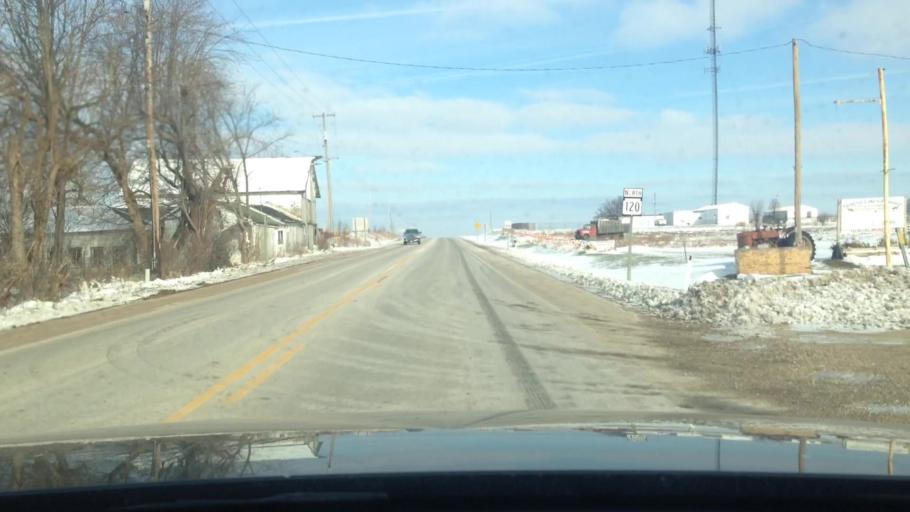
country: US
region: Wisconsin
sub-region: Walworth County
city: East Troy
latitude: 42.6915
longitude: -88.4047
